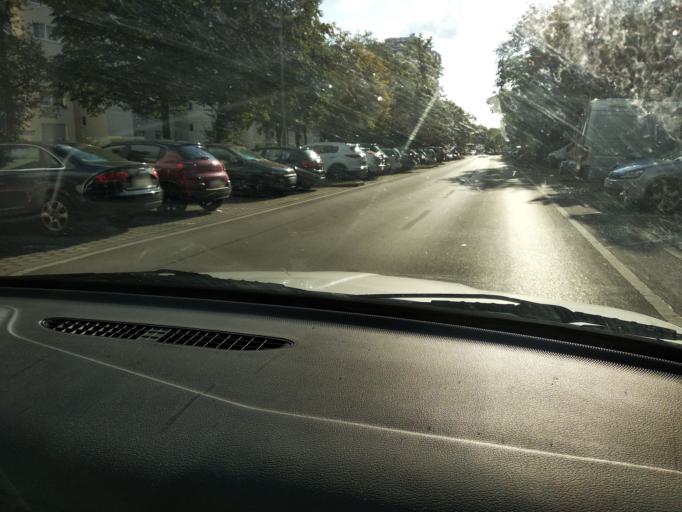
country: DE
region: Bavaria
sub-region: Upper Bavaria
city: Taufkirchen
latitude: 48.0545
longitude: 11.6030
